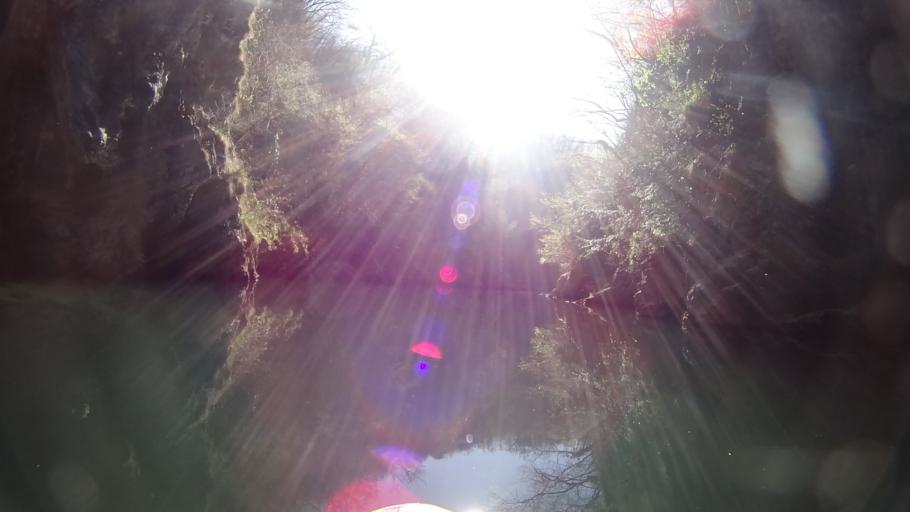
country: IT
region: Veneto
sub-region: Provincia di Vicenza
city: Cogollo del Cengio
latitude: 45.7779
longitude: 11.4151
